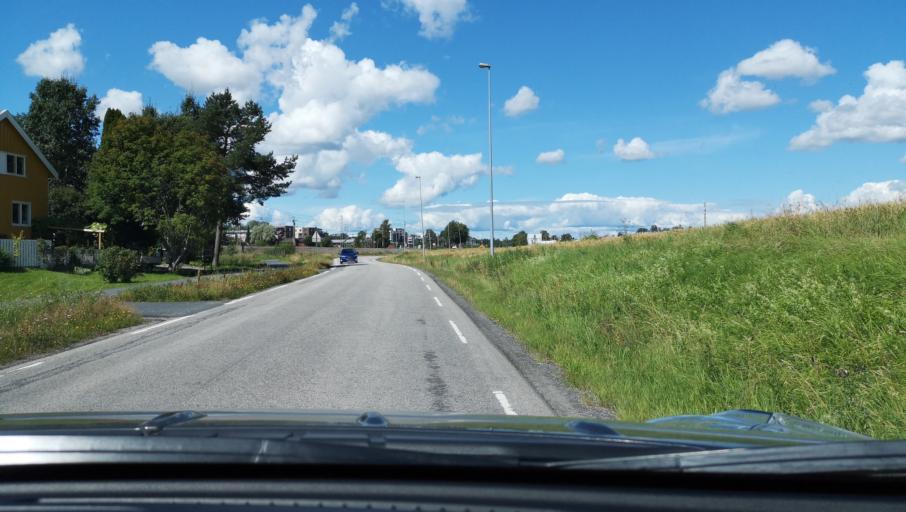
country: NO
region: Akershus
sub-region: As
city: As
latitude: 59.6576
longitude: 10.7985
